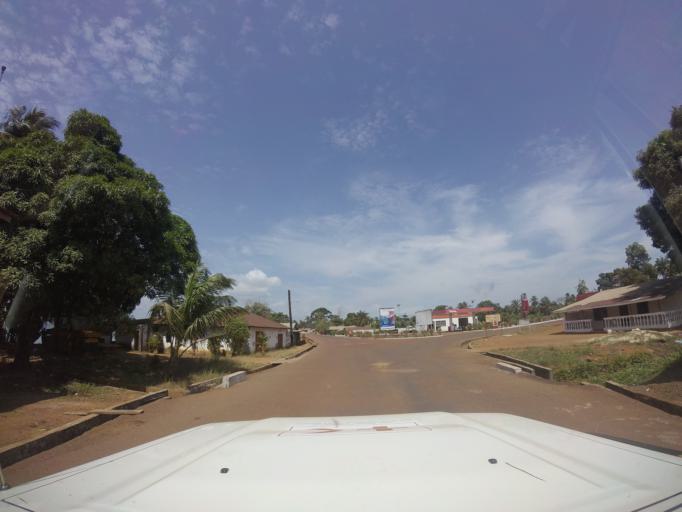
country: LR
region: Grand Cape Mount
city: Robertsport
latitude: 6.7541
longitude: -11.3644
